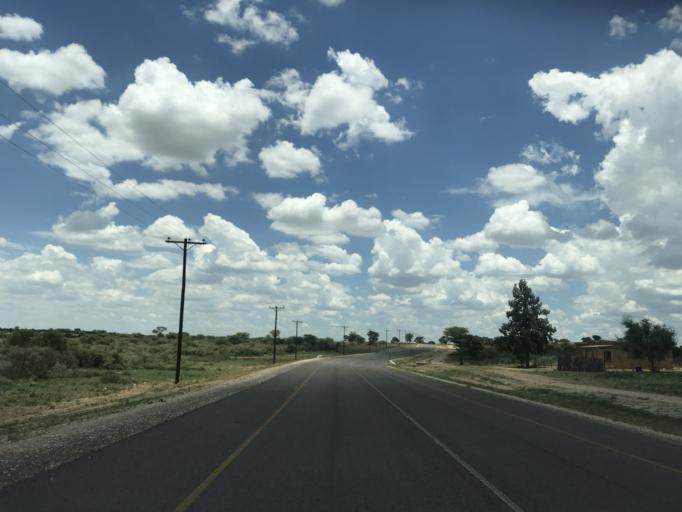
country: BW
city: Mabuli
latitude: -25.7304
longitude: 24.9984
